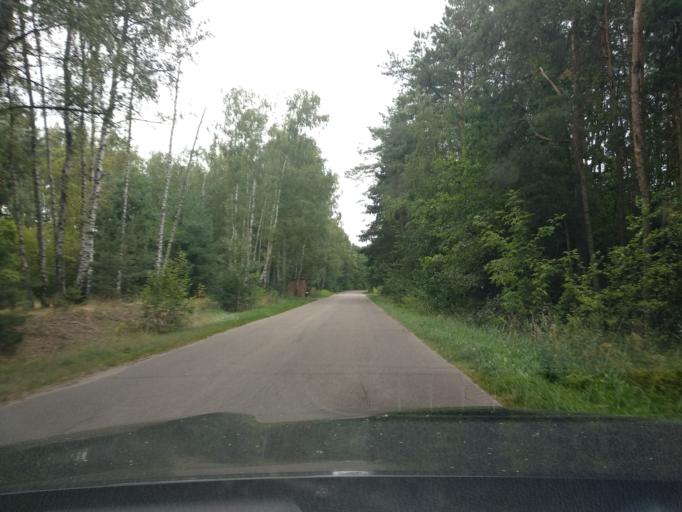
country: PL
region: Masovian Voivodeship
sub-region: Powiat pultuski
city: Obryte
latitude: 52.7428
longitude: 21.2164
